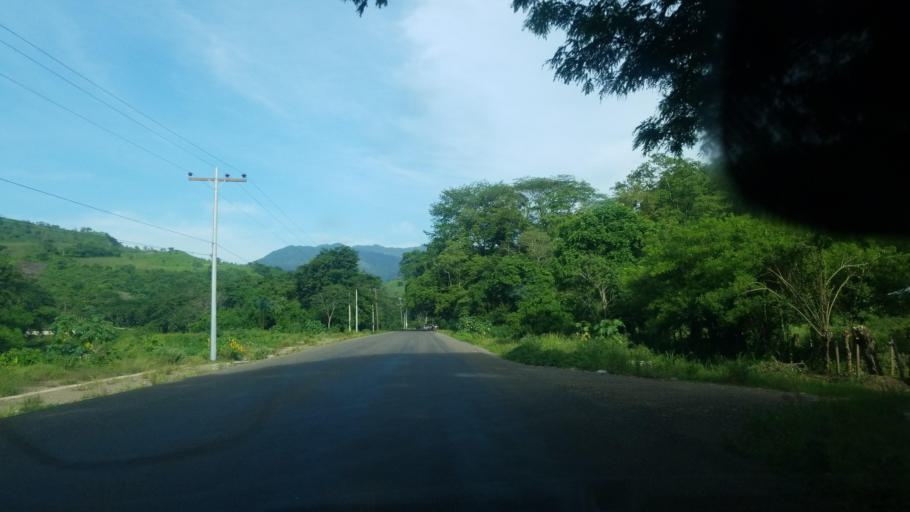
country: HN
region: Santa Barbara
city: Trinidad
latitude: 15.1322
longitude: -88.2144
